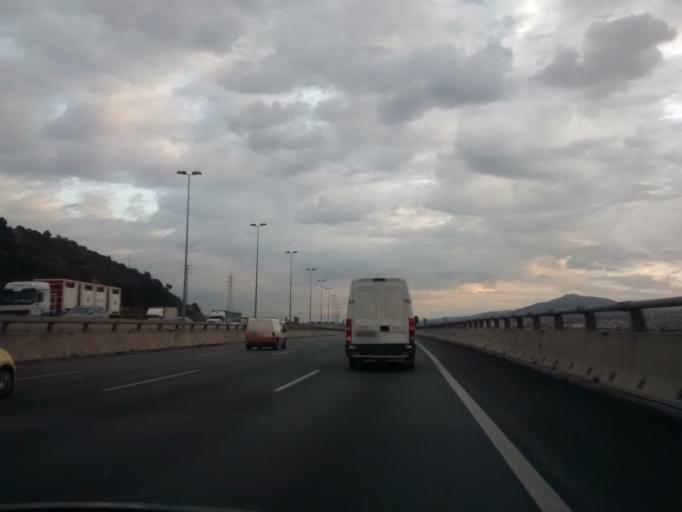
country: ES
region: Catalonia
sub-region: Provincia de Barcelona
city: Palleja
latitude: 41.4251
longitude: 2.0062
